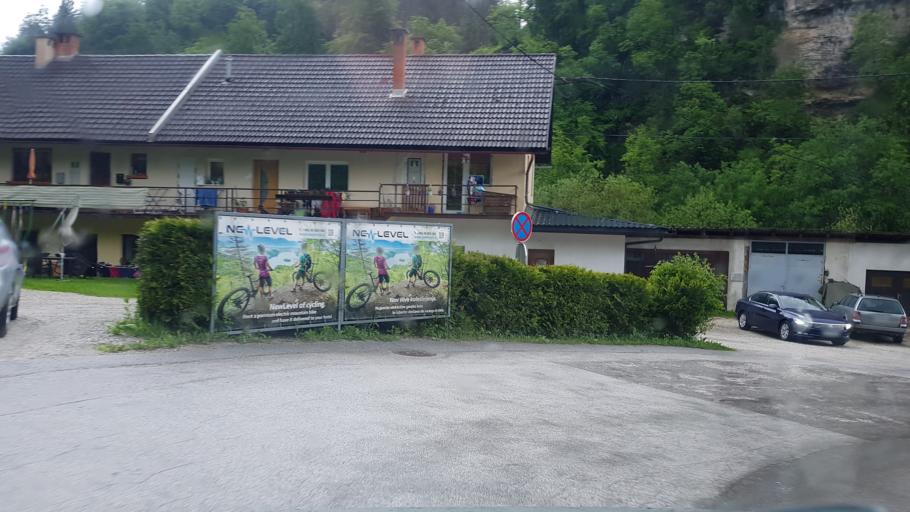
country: SI
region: Gorje
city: Zgornje Gorje
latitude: 46.3902
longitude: 14.0837
